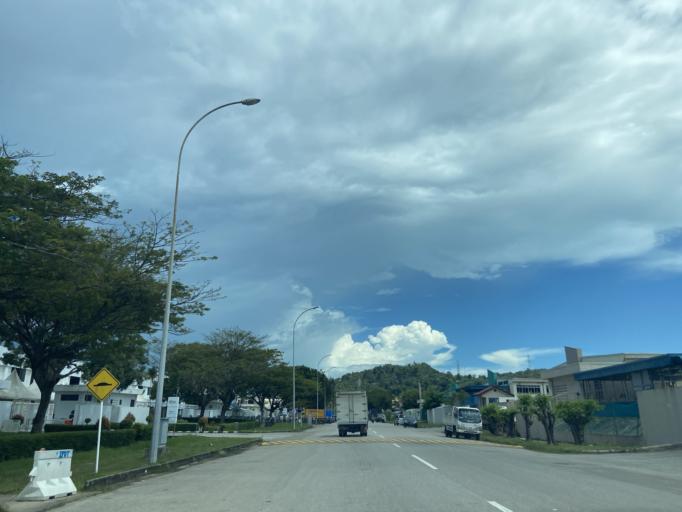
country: SG
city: Singapore
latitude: 1.0588
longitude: 104.0366
